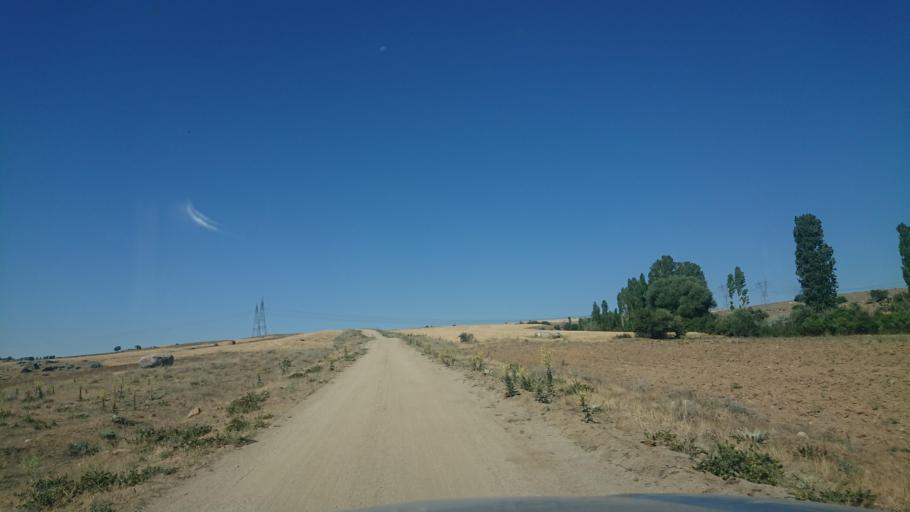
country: TR
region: Aksaray
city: Sariyahsi
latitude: 38.9421
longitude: 33.8736
